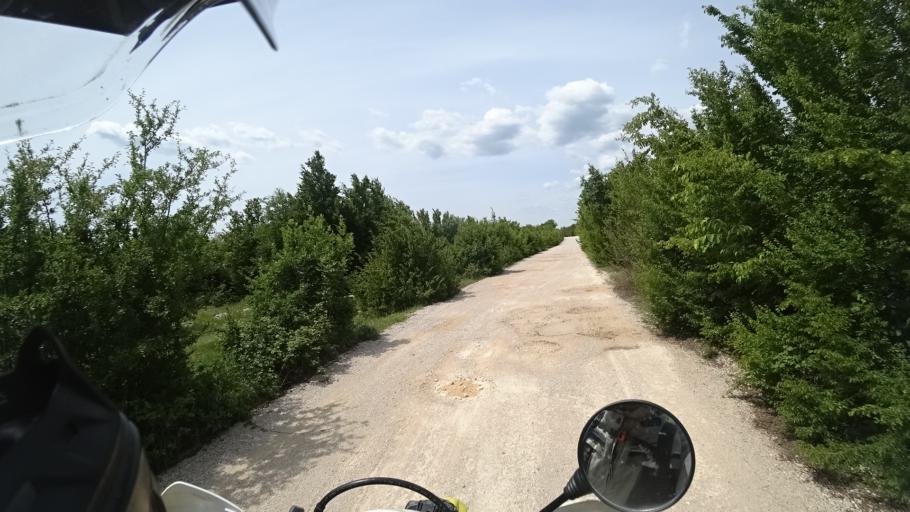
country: HR
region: Sibensko-Kniniska
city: Kistanje
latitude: 44.0576
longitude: 16.0376
